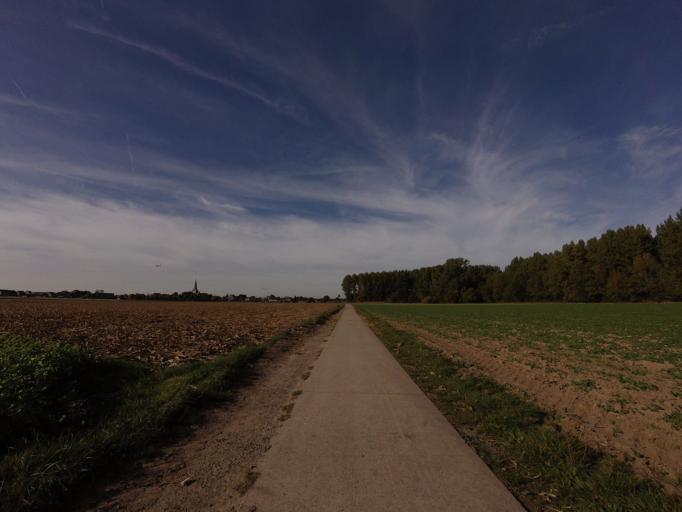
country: BE
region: Flanders
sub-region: Provincie Vlaams-Brabant
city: Kampenhout
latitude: 50.9156
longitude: 4.5718
